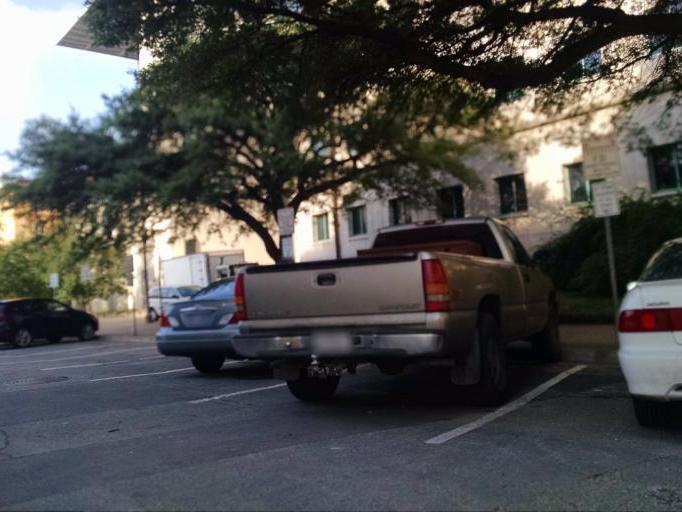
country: US
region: Texas
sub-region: Travis County
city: Austin
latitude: 30.2881
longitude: -97.7369
